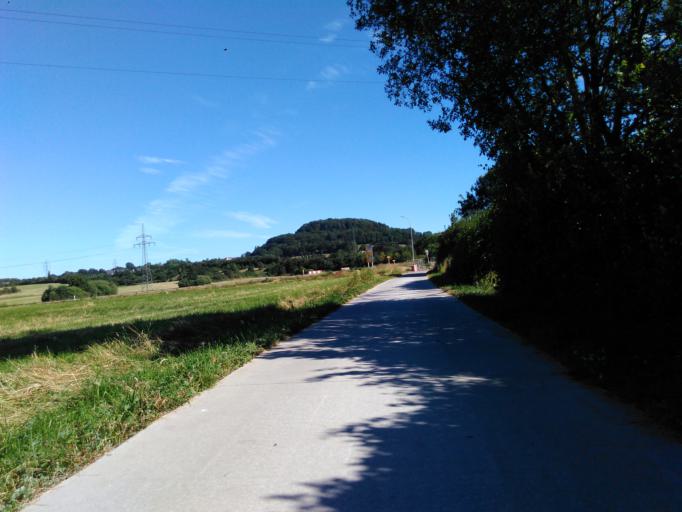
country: LU
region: Luxembourg
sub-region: Canton d'Esch-sur-Alzette
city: Sanem
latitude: 49.5368
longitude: 5.9290
